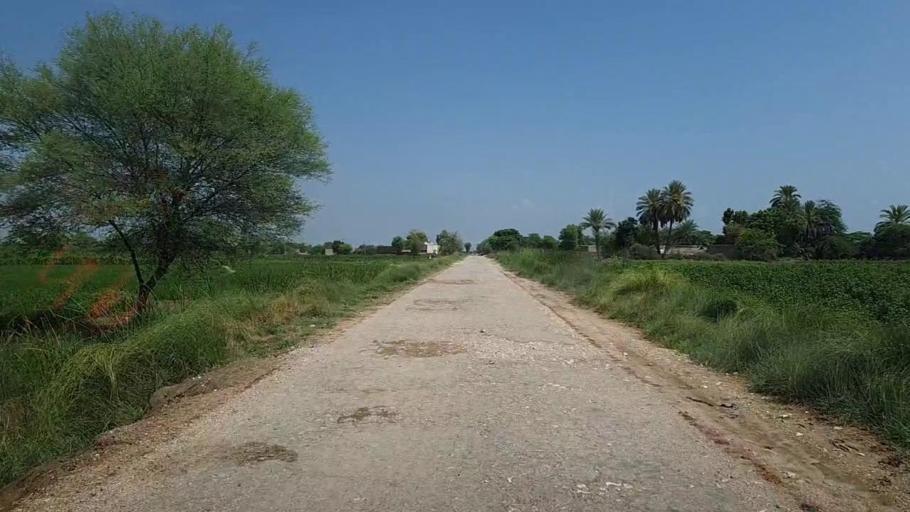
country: PK
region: Sindh
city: Bhiria
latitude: 26.8882
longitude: 68.2311
